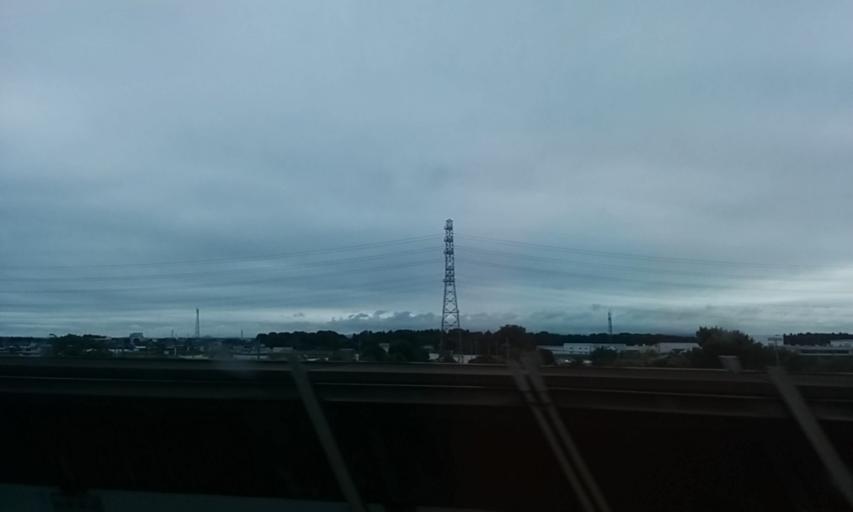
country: JP
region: Tochigi
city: Kaminokawa
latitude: 36.4213
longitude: 139.8640
